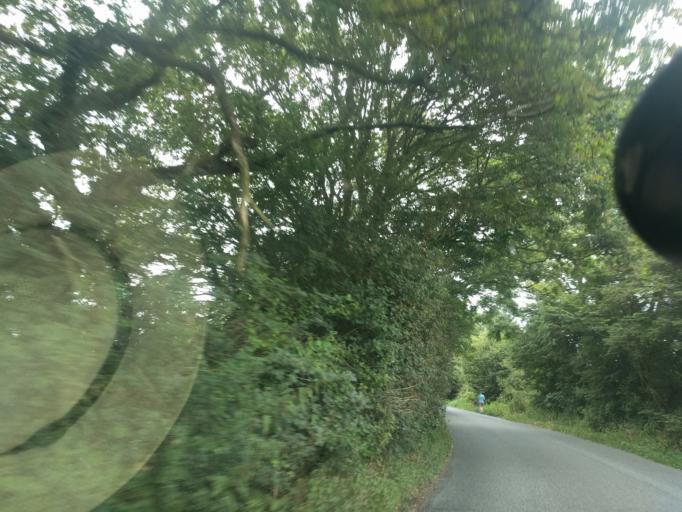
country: GB
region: England
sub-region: Wiltshire
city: Lacock
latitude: 51.3974
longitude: -2.1012
